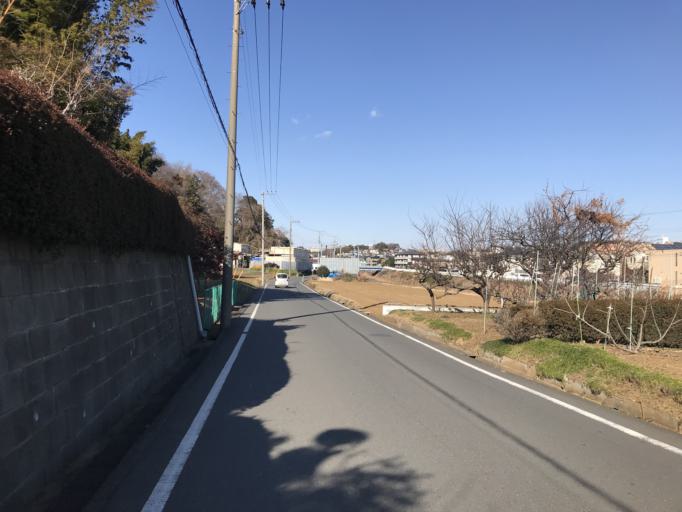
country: JP
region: Tokyo
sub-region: Machida-shi
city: Machida
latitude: 35.5723
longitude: 139.5088
